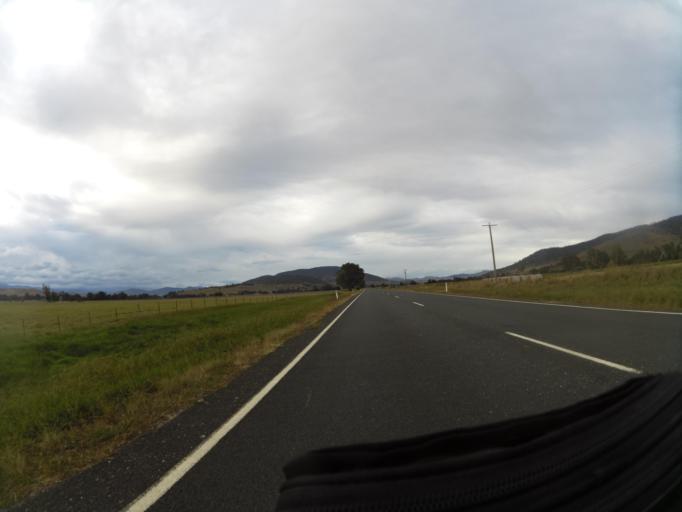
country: AU
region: New South Wales
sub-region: Snowy River
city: Jindabyne
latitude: -36.1006
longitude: 147.9812
